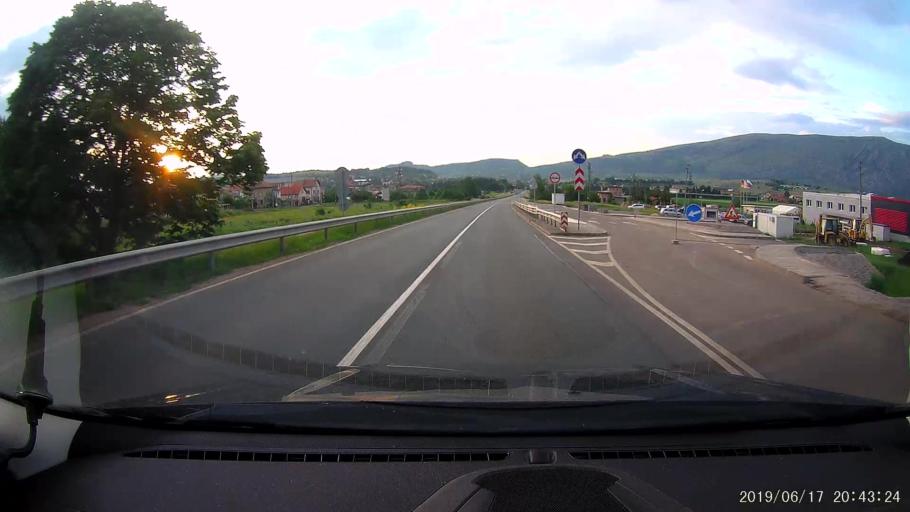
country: BG
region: Sofiya
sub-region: Obshtina Dragoman
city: Dragoman
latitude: 42.9147
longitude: 22.9406
